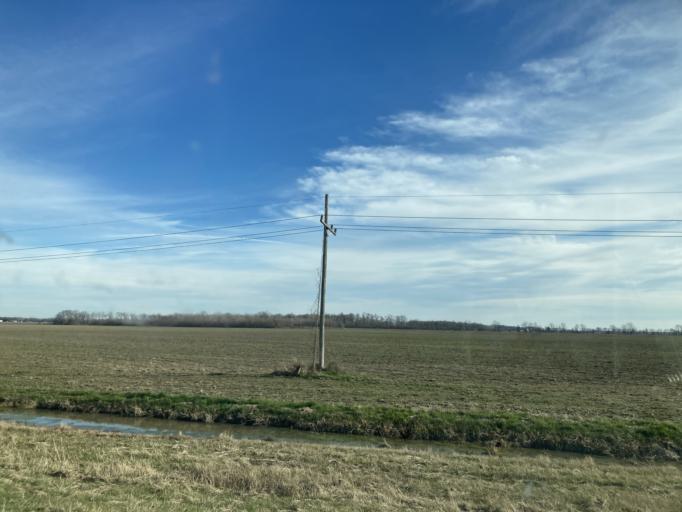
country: US
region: Mississippi
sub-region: Humphreys County
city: Belzoni
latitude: 32.9889
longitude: -90.5883
